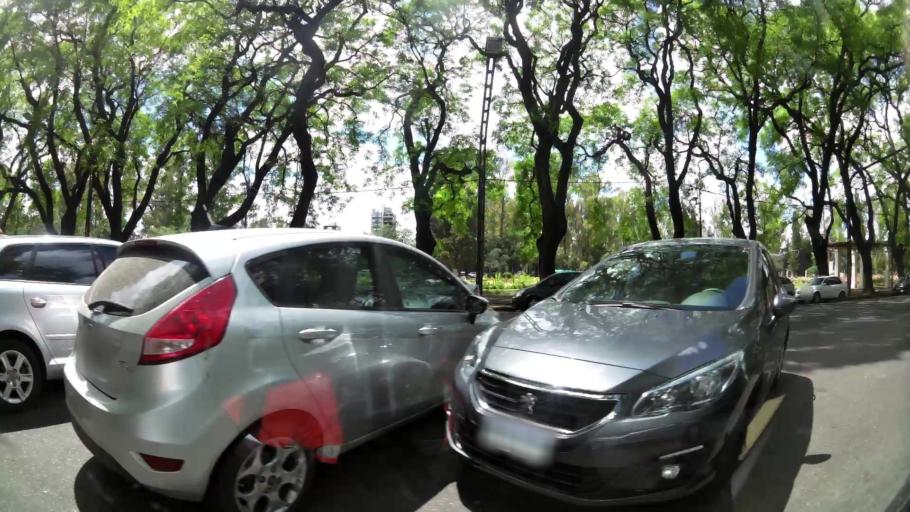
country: AR
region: Santa Fe
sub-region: Departamento de Rosario
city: Rosario
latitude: -32.9591
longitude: -60.6572
